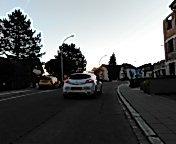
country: LU
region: Luxembourg
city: Soleuvre
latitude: 49.5197
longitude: 5.9375
